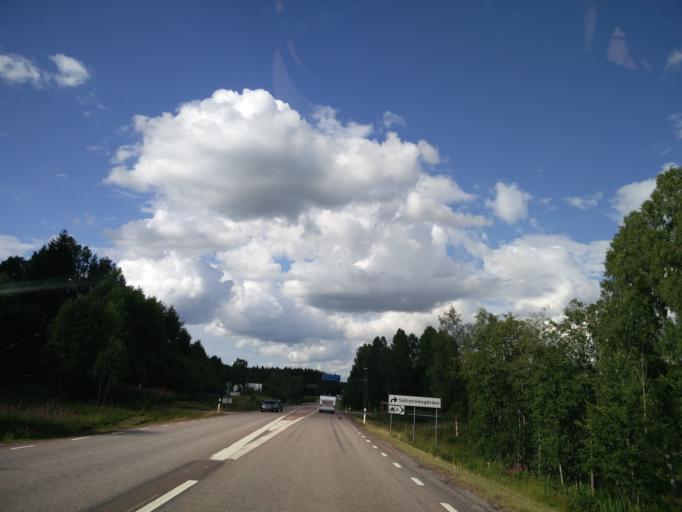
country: SE
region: Vaermland
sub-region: Torsby Kommun
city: Torsby
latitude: 60.1547
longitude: 13.0021
